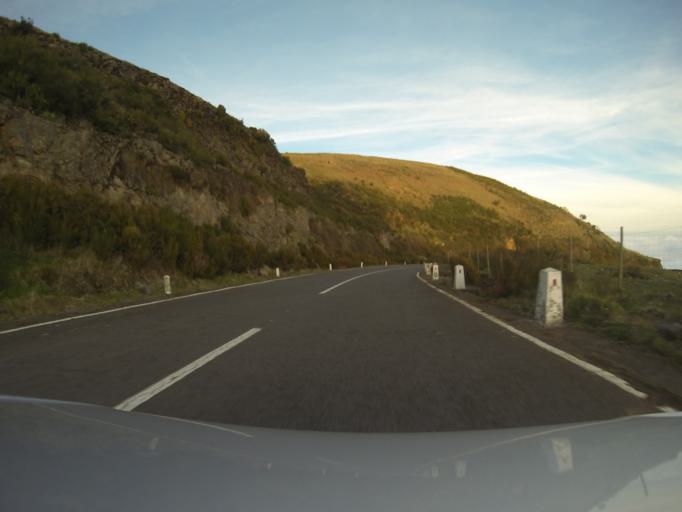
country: PT
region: Madeira
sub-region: Sao Vicente
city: Sao Vicente
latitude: 32.7330
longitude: -17.0575
